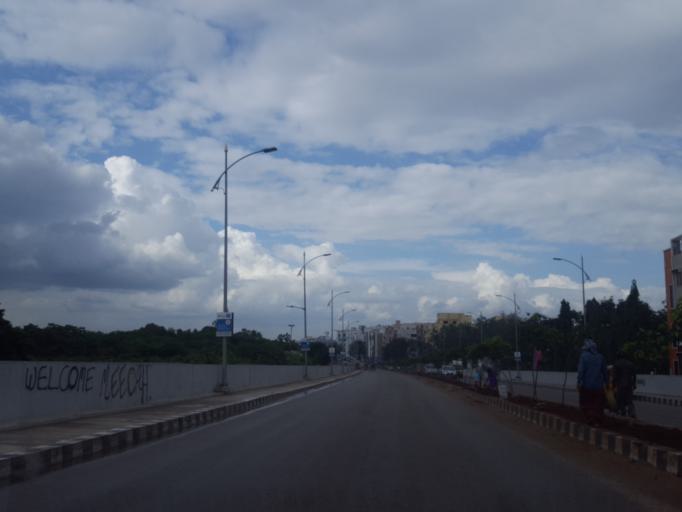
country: IN
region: Telangana
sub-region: Medak
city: Serilingampalle
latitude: 17.4838
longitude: 78.3118
